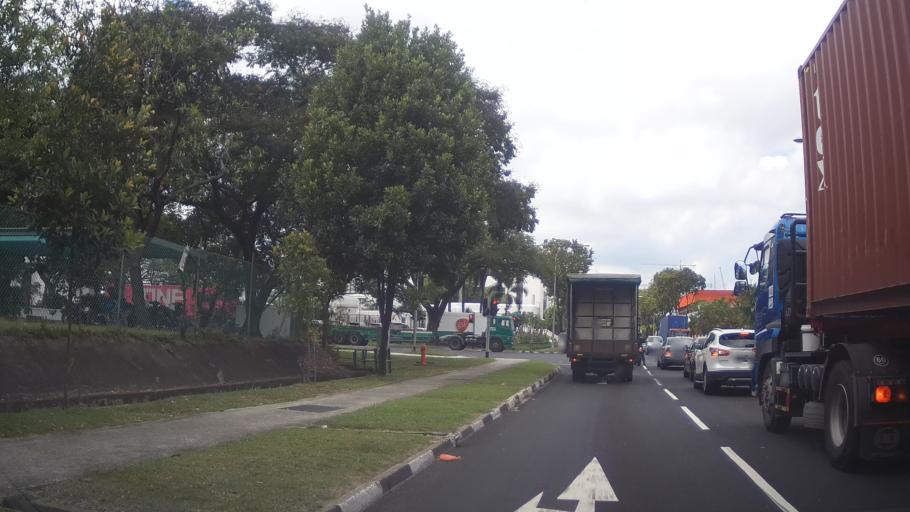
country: MY
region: Johor
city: Johor Bahru
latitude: 1.3105
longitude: 103.6609
